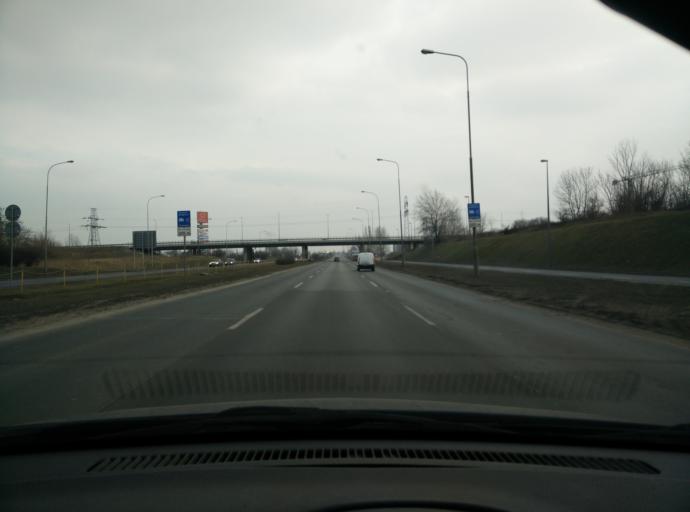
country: PL
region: Greater Poland Voivodeship
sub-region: Poznan
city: Poznan
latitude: 52.3811
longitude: 16.9761
